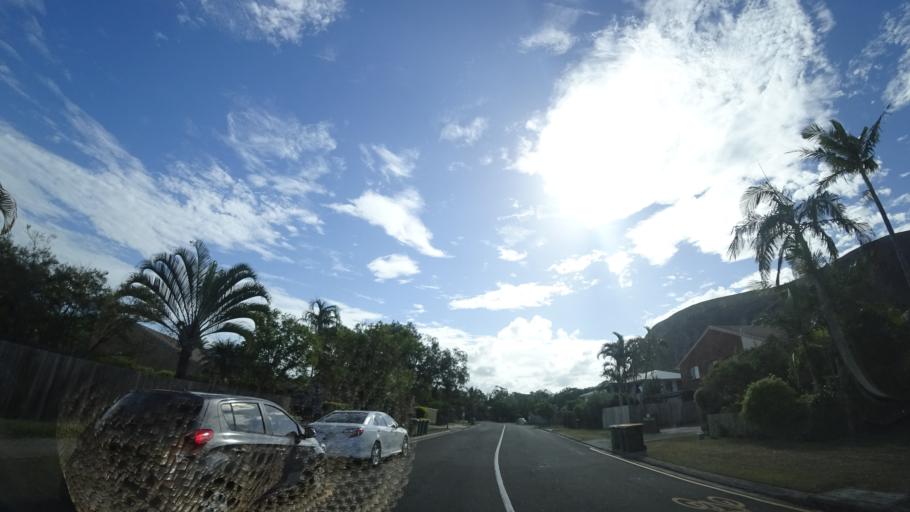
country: AU
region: Queensland
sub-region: Sunshine Coast
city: Coolum Beach
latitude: -26.5642
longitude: 153.0911
